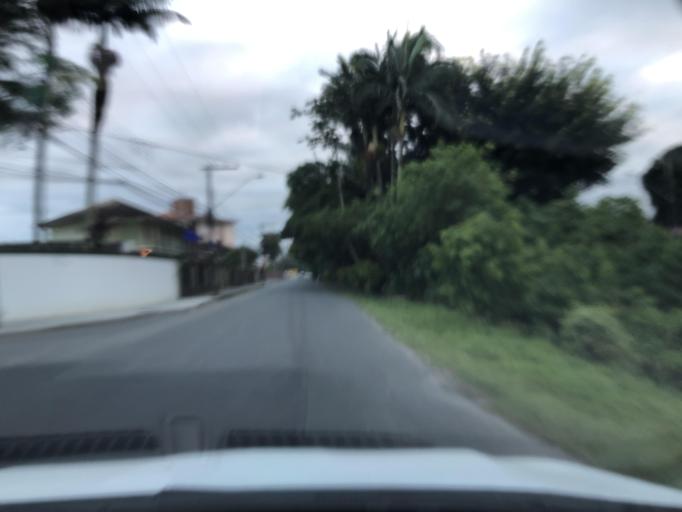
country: BR
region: Santa Catarina
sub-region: Joinville
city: Joinville
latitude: -26.2719
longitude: -48.8698
